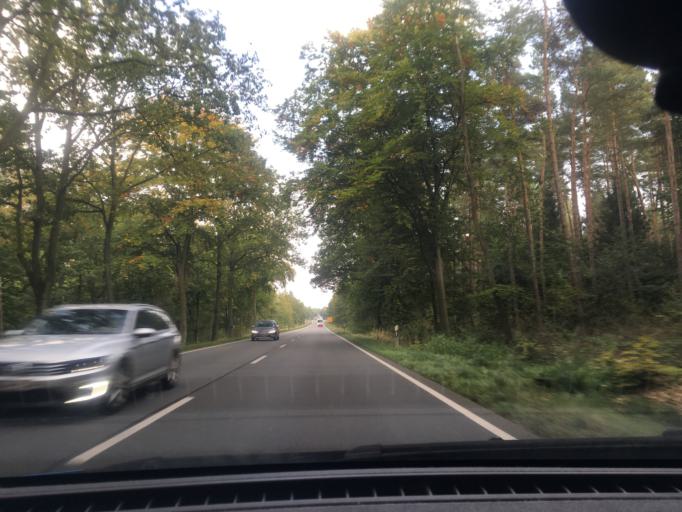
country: DE
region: Lower Saxony
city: Reinstorf
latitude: 53.2230
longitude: 10.5587
